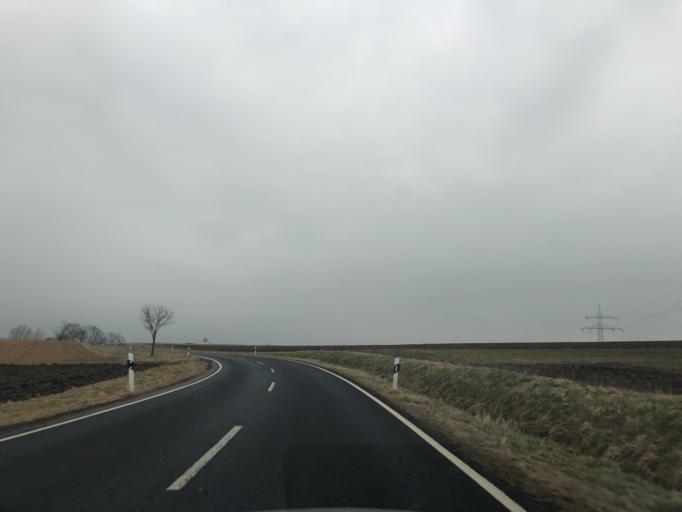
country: DE
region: Hesse
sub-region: Regierungsbezirk Darmstadt
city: Birstein
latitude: 50.3747
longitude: 9.3007
